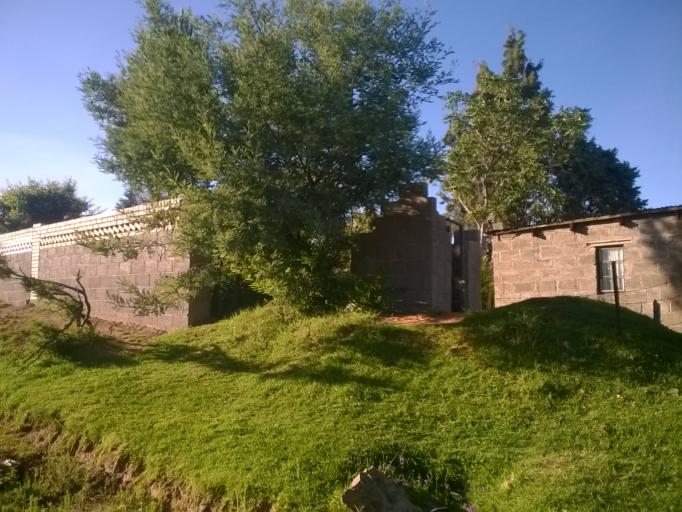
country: LS
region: Maseru
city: Maseru
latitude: -29.2885
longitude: 27.5280
